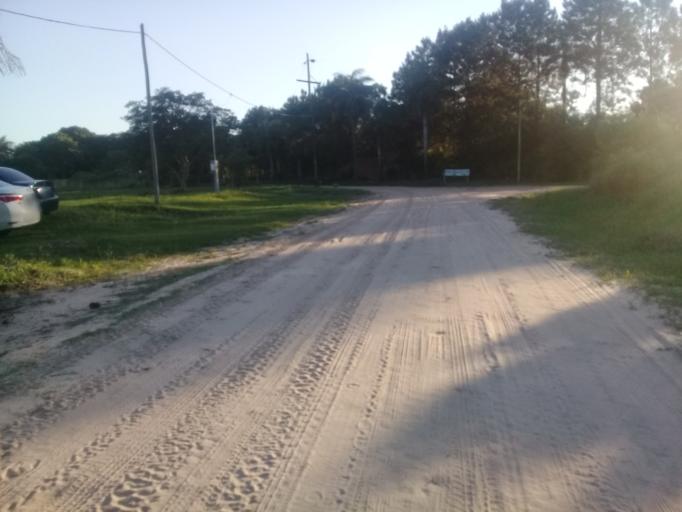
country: AR
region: Corrientes
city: San Luis del Palmar
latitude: -27.4678
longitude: -58.6633
